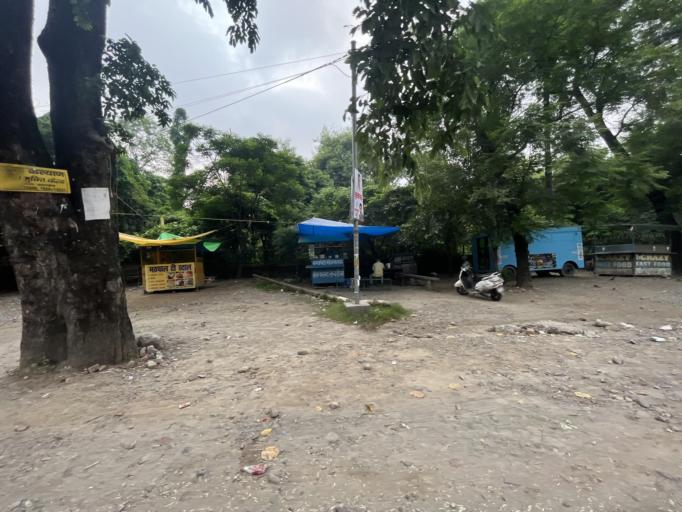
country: IN
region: Uttarakhand
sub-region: Naini Tal
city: Haldwani
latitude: 29.2045
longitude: 79.5172
